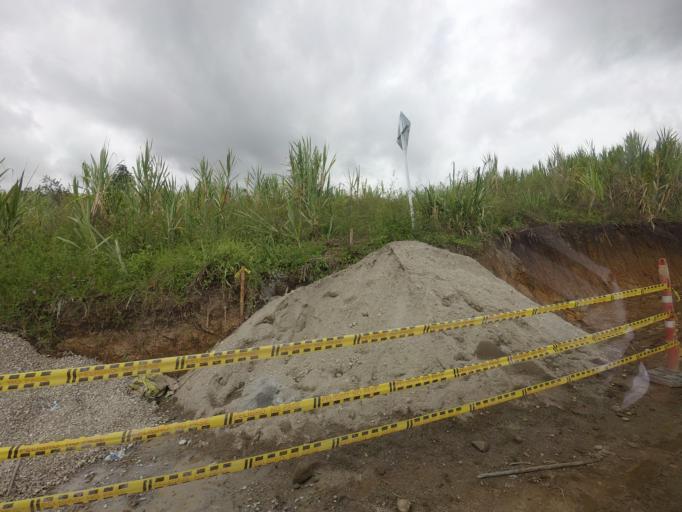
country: CO
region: Huila
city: San Agustin
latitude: 1.9435
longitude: -76.2975
